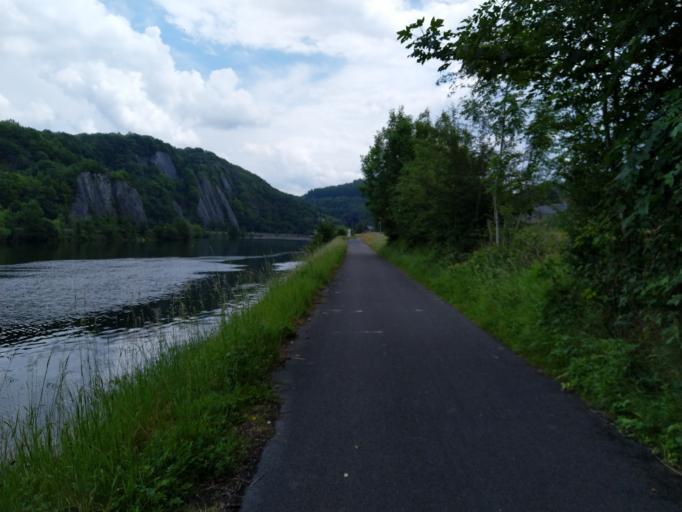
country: BE
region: Wallonia
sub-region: Province de Namur
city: Yvoir
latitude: 50.3382
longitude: 4.8638
